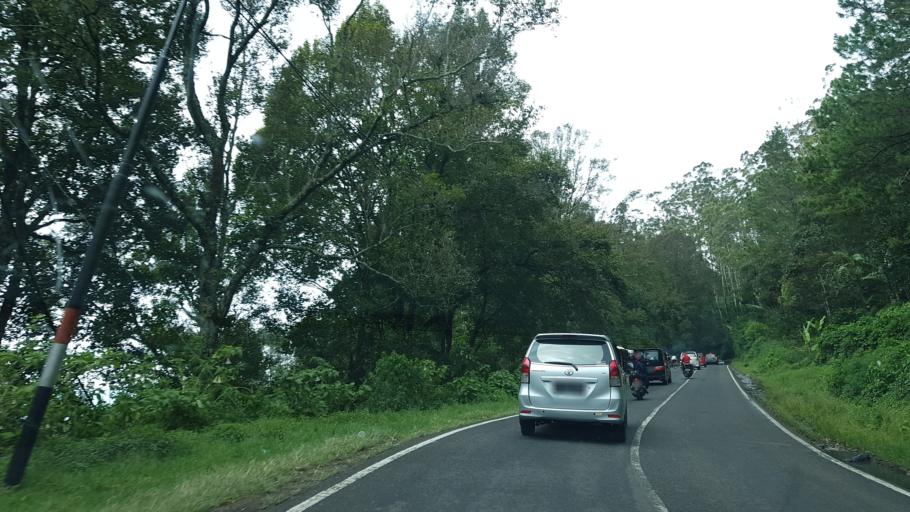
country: ID
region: West Java
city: Banjar
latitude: -7.1348
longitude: 107.4082
